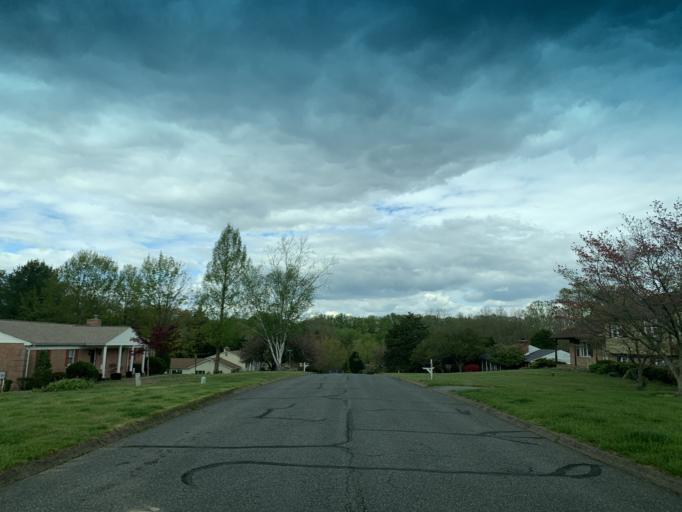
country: US
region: Maryland
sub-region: Harford County
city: Pleasant Hills
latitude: 39.4965
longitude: -76.3615
